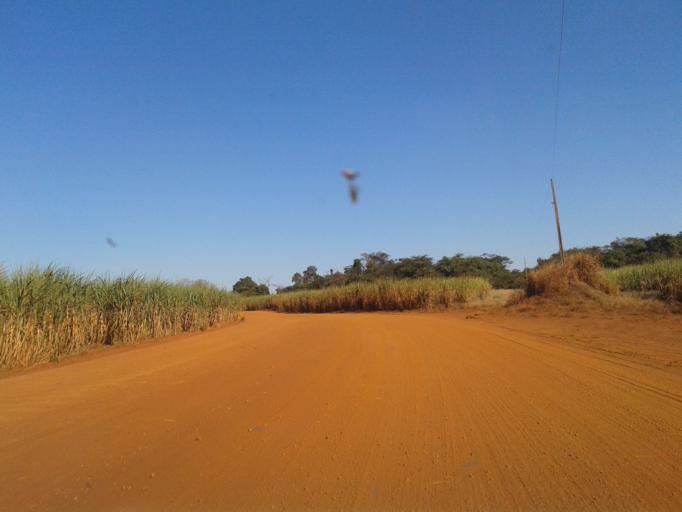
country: BR
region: Minas Gerais
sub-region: Santa Vitoria
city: Santa Vitoria
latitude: -18.8711
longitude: -50.0495
